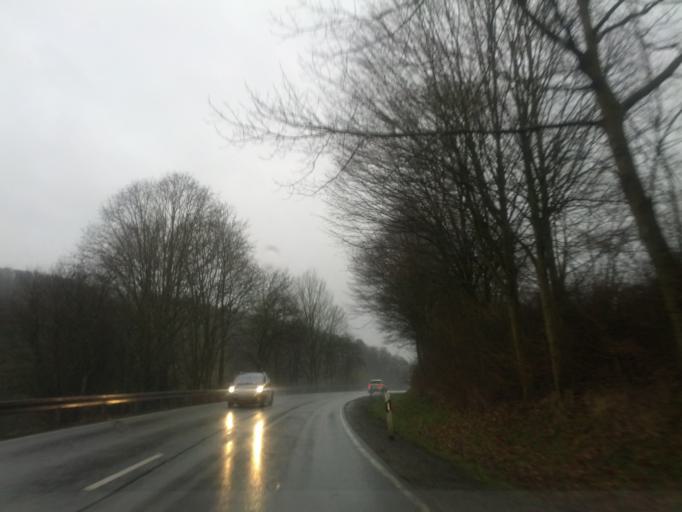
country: DE
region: Hesse
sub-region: Regierungsbezirk Kassel
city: Sontra
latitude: 51.0941
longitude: 9.9745
